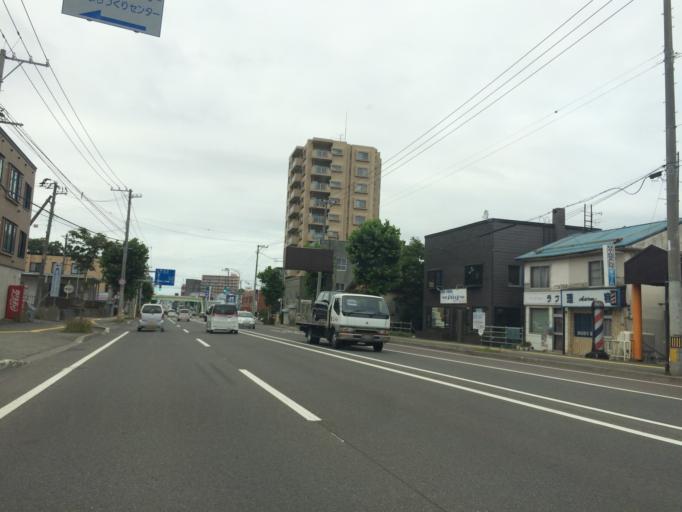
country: JP
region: Hokkaido
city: Sapporo
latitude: 43.1149
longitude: 141.2444
